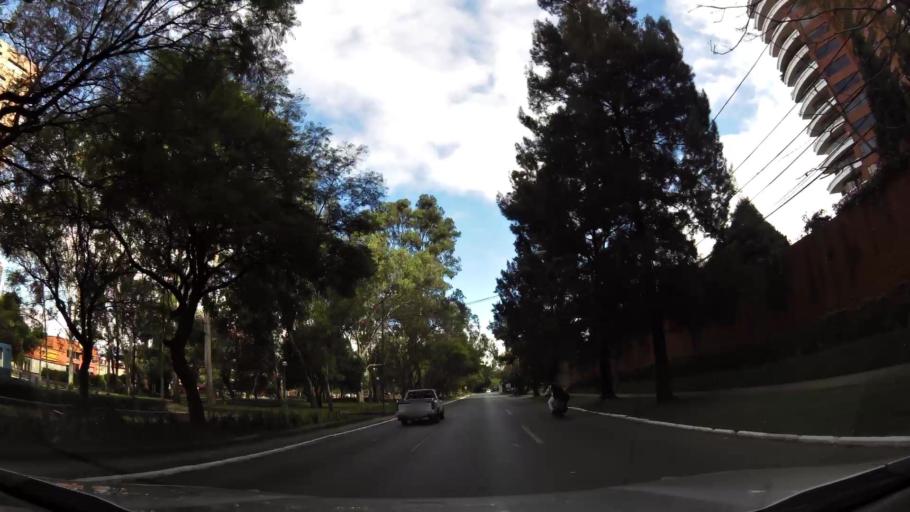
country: GT
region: Guatemala
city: Santa Catarina Pinula
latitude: 14.5877
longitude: -90.5200
